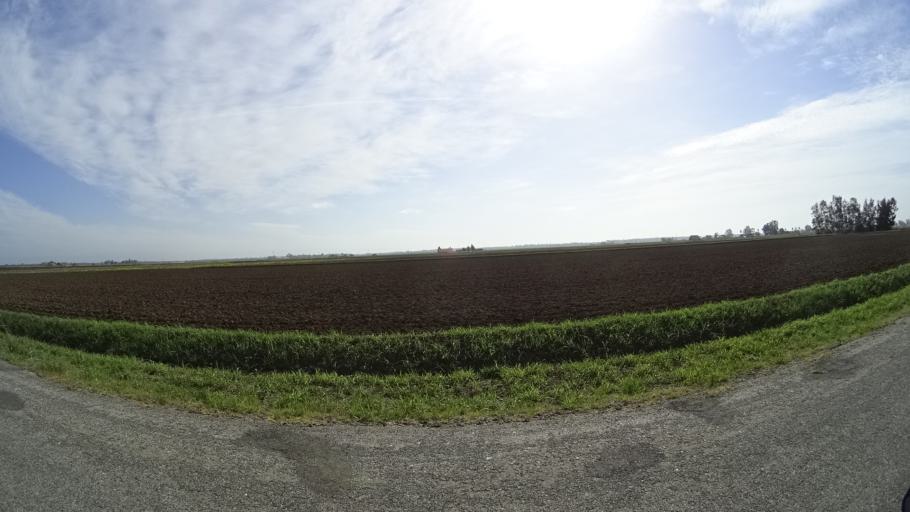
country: US
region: California
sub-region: Glenn County
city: Hamilton City
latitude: 39.5998
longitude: -122.0467
